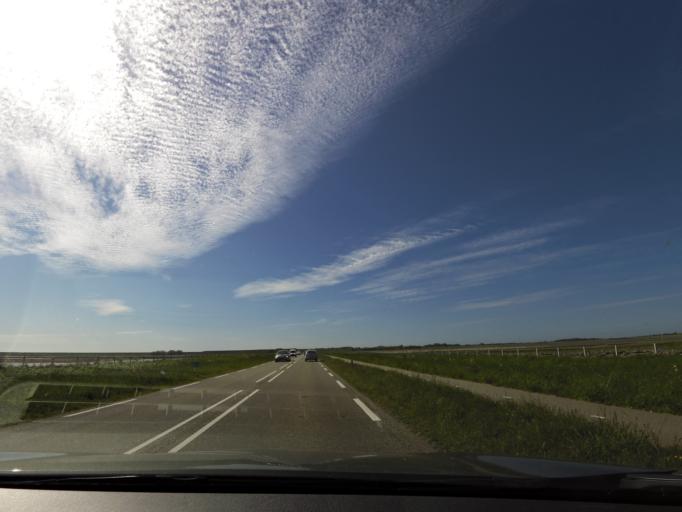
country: NL
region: Zeeland
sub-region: Schouwen-Duiveland
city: Scharendijke
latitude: 51.6904
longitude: 3.8409
